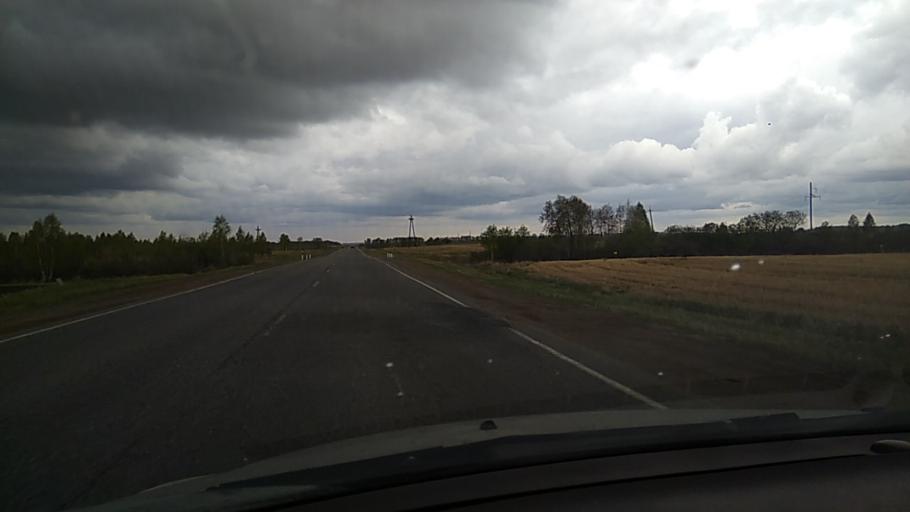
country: RU
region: Kurgan
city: Dalmatovo
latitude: 56.2897
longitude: 62.8541
